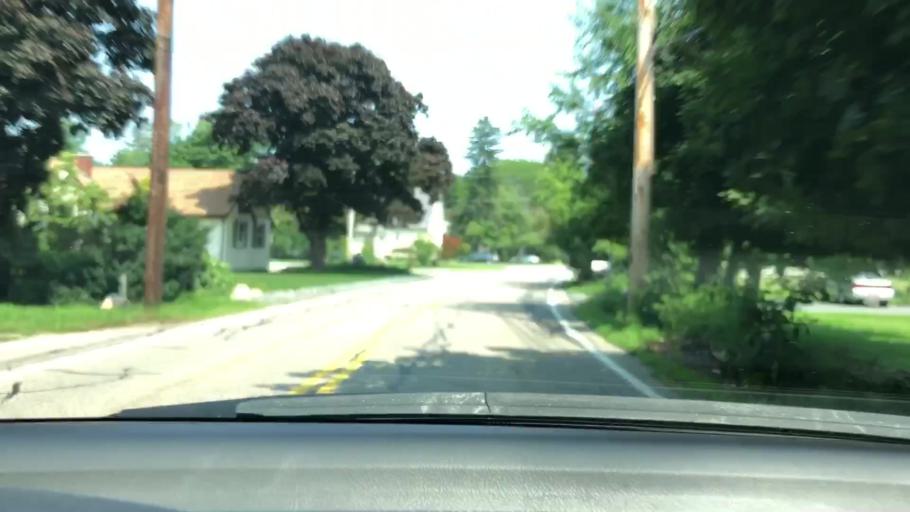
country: US
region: Massachusetts
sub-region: Norfolk County
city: Dedham
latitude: 42.2145
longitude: -71.1668
